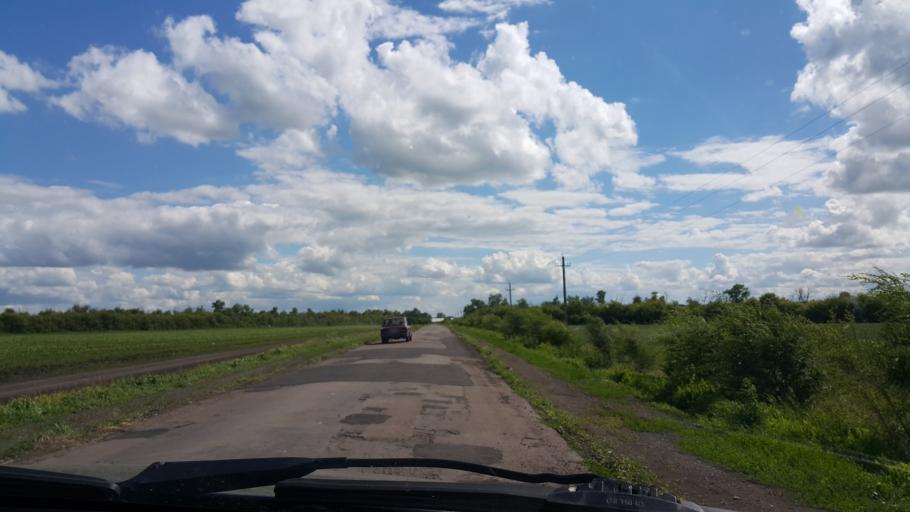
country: RU
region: Tambov
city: Satinka
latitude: 52.3931
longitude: 41.6640
